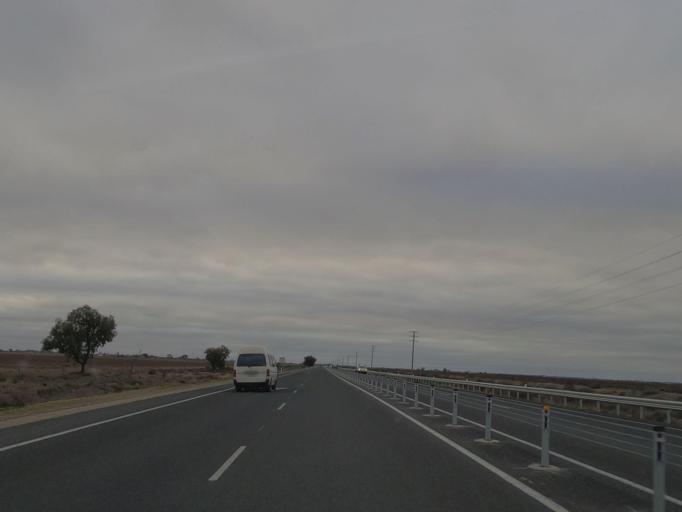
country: AU
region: Victoria
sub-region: Swan Hill
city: Swan Hill
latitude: -35.5084
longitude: 143.7224
